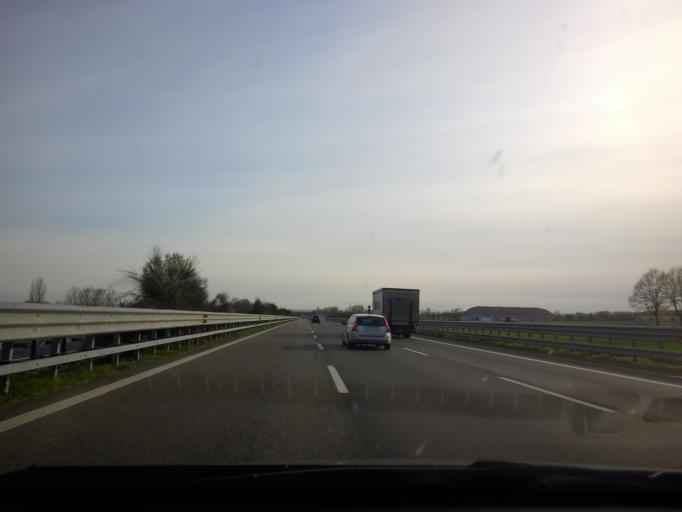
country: IT
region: Lombardy
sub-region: Provincia di Brescia
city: Leno
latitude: 45.3809
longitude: 10.1776
